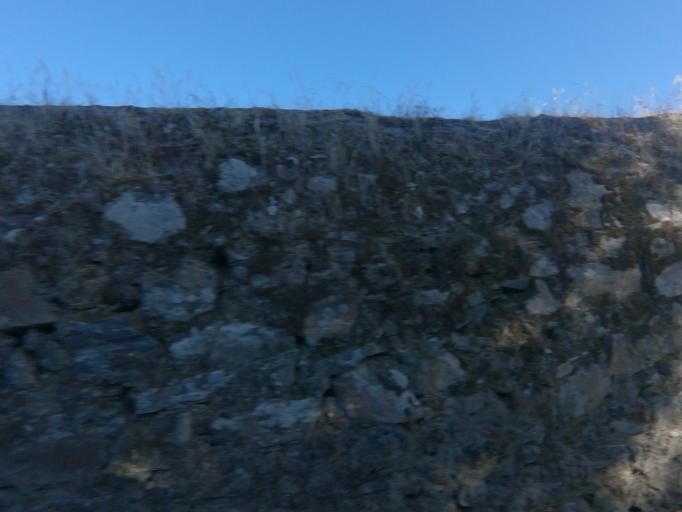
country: PT
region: Vila Real
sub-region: Peso da Regua
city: Peso da Regua
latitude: 41.1762
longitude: -7.7812
